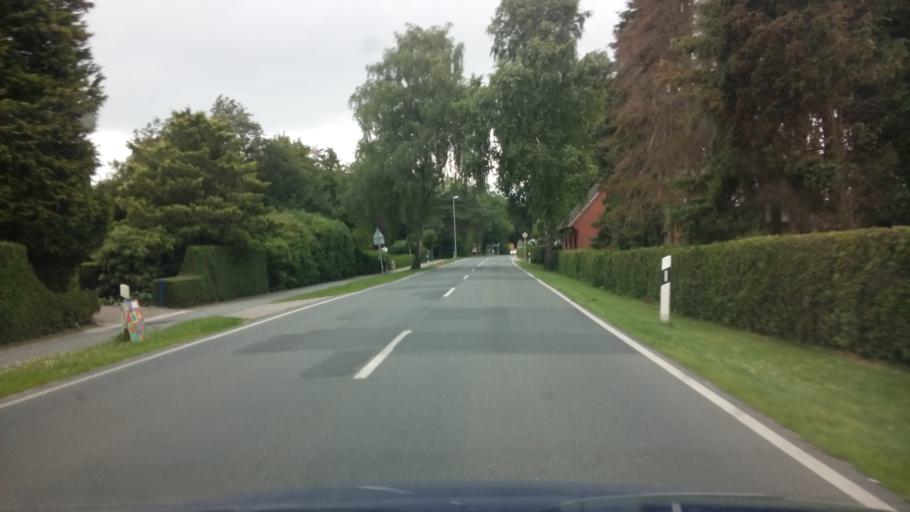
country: DE
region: Lower Saxony
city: Worpswede
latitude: 53.2068
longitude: 8.9306
